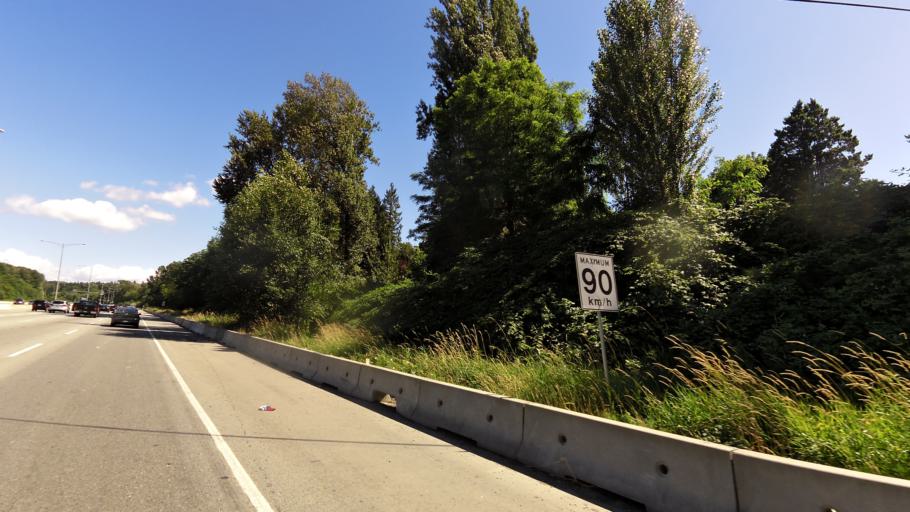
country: CA
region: British Columbia
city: Burnaby
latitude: 49.2398
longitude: -122.9552
